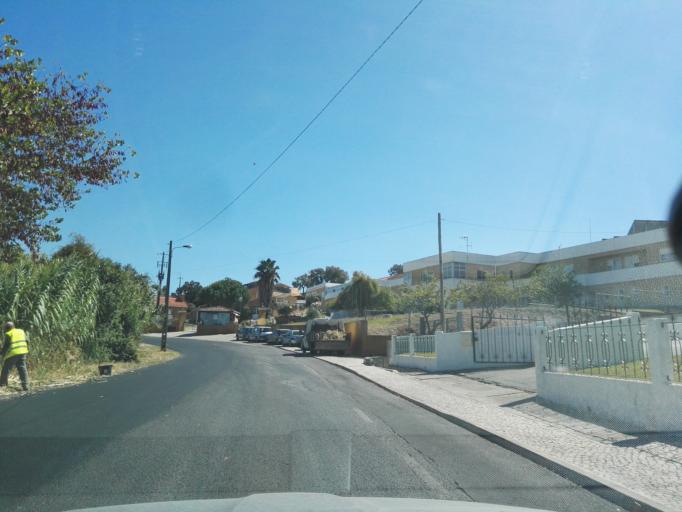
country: PT
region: Lisbon
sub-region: Arruda Dos Vinhos
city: Arruda dos Vinhos
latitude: 38.9781
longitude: -9.0764
